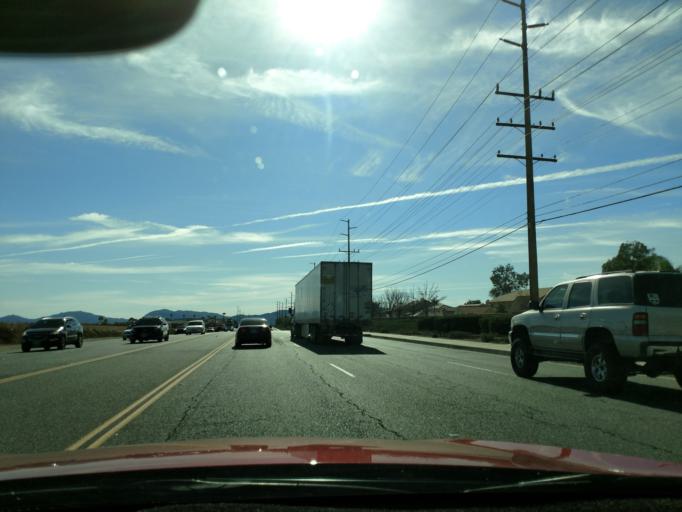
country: US
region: California
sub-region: Riverside County
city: Murrieta Hot Springs
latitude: 33.5670
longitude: -117.1371
